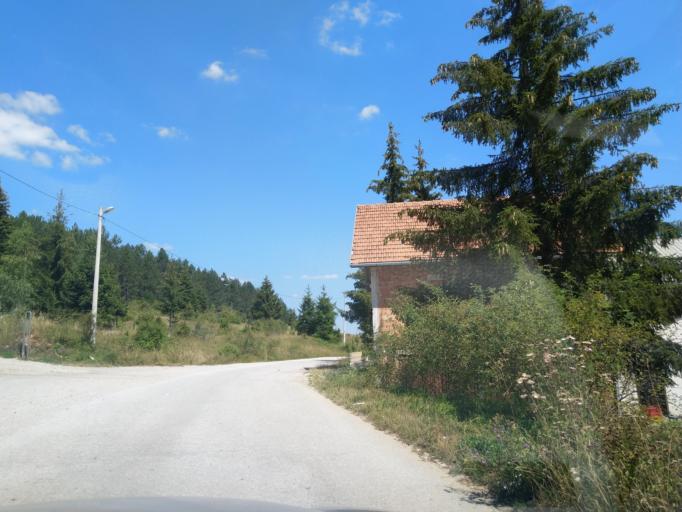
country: RS
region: Central Serbia
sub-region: Zlatiborski Okrug
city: Nova Varos
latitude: 43.4665
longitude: 19.9720
